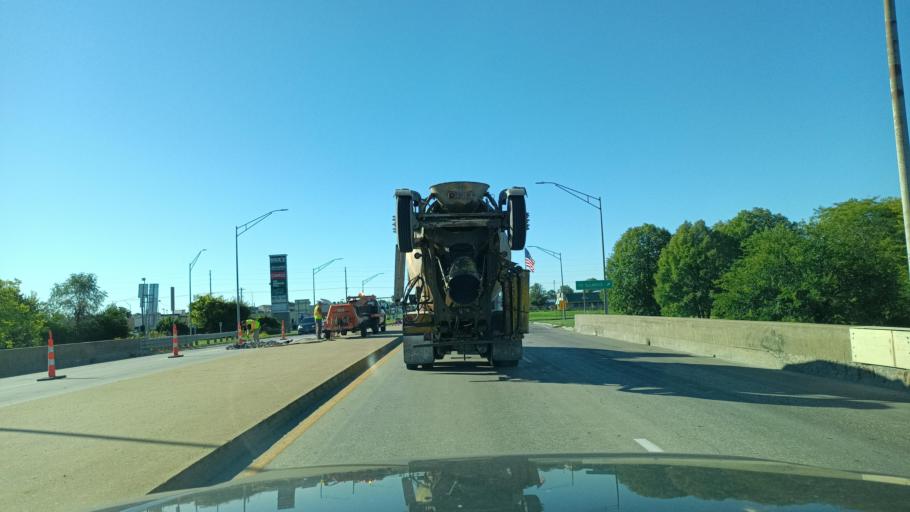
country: US
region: Iowa
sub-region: Des Moines County
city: West Burlington
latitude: 40.8176
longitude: -91.1415
